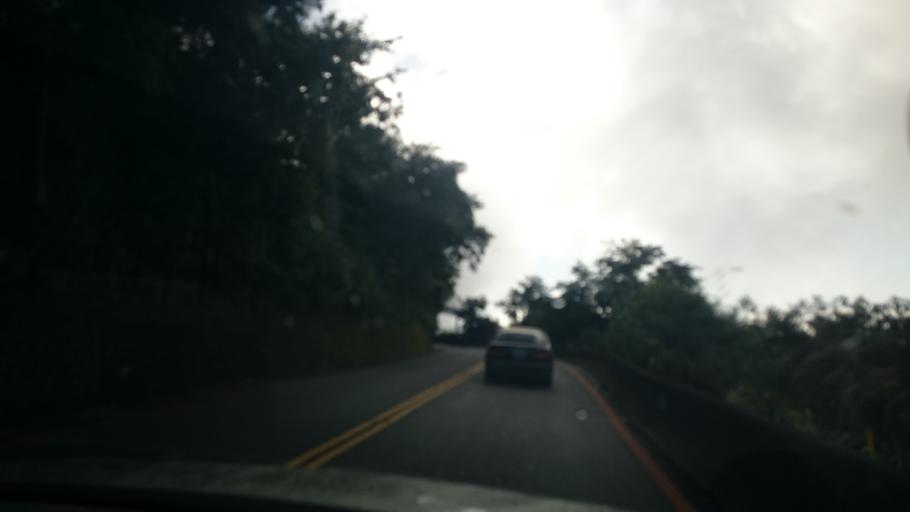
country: TW
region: Taiwan
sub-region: Nantou
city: Puli
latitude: 24.0496
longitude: 121.1598
